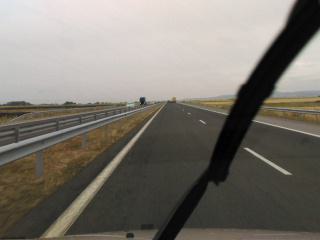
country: BG
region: Sliven
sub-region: Obshtina Nova Zagora
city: Nova Zagora
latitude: 42.4197
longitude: 25.9456
